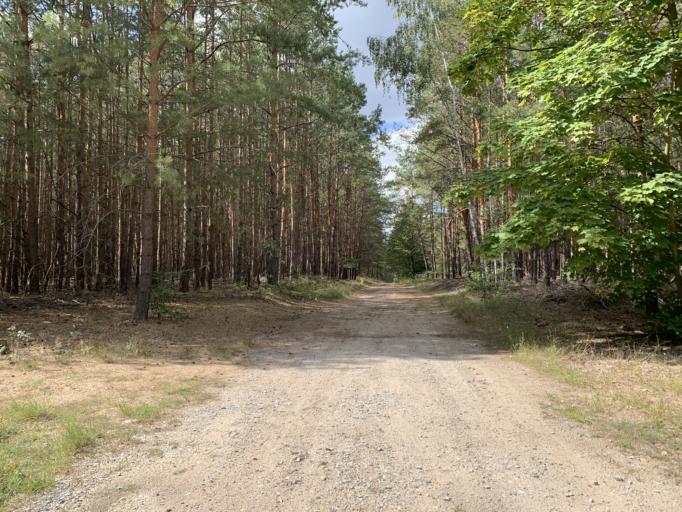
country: DE
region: Brandenburg
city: Michendorf
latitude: 52.3195
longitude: 13.0002
